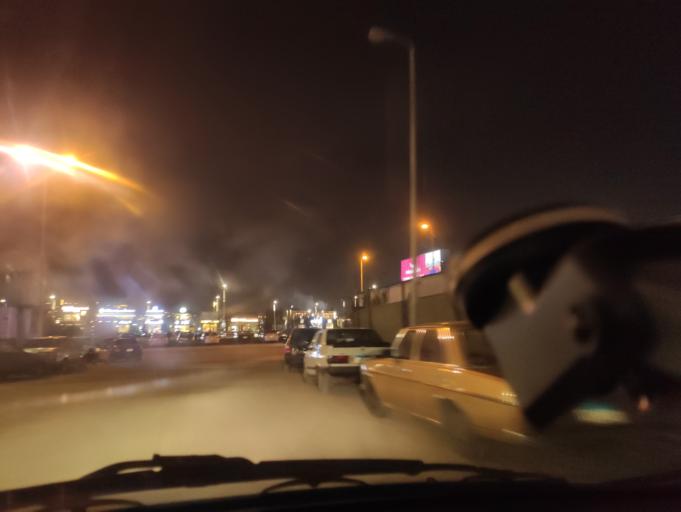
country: EG
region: Al Jizah
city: Awsim
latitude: 30.0179
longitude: 31.0035
